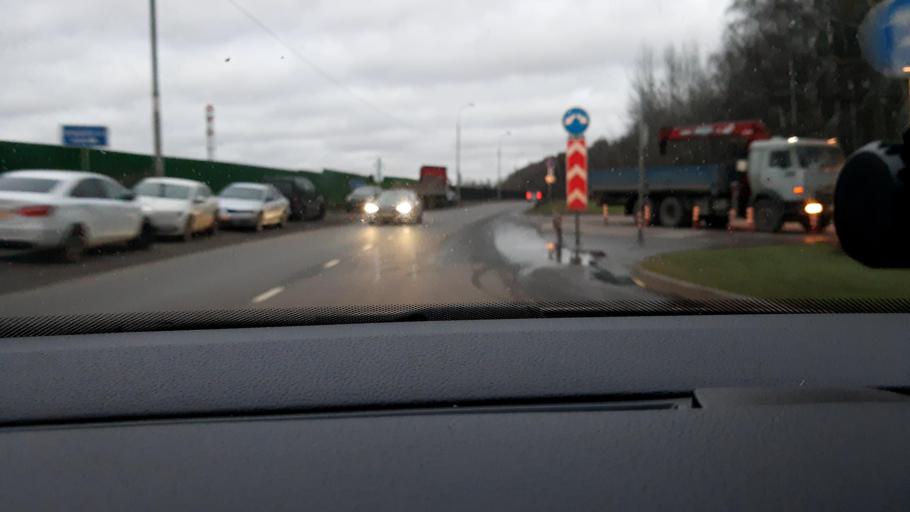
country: RU
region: Moskovskaya
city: Zarech'ye
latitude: 55.6799
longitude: 37.3960
